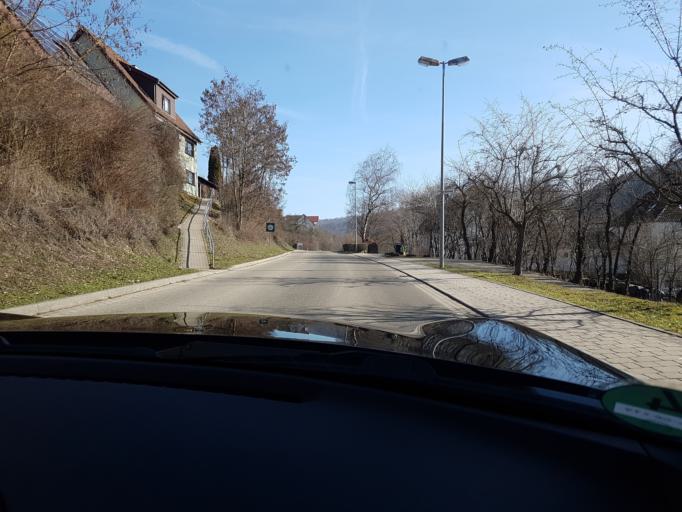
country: DE
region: Baden-Wuerttemberg
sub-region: Regierungsbezirk Stuttgart
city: Krautheim
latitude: 49.3776
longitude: 9.6423
